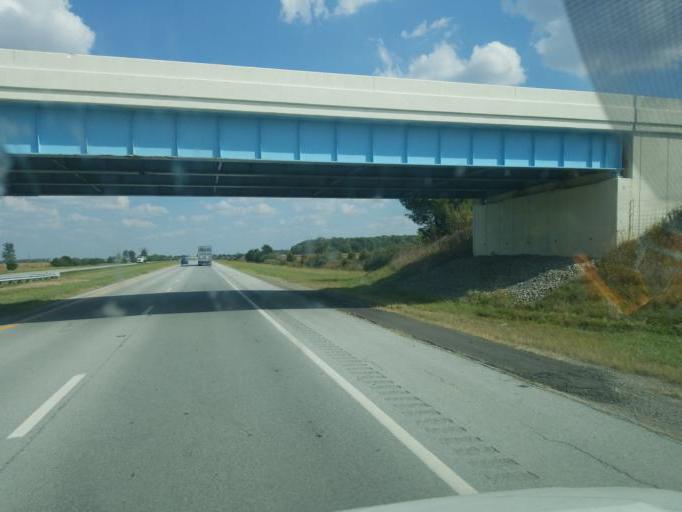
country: US
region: Ohio
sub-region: Allen County
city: Delphos
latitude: 40.8732
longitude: -84.3986
